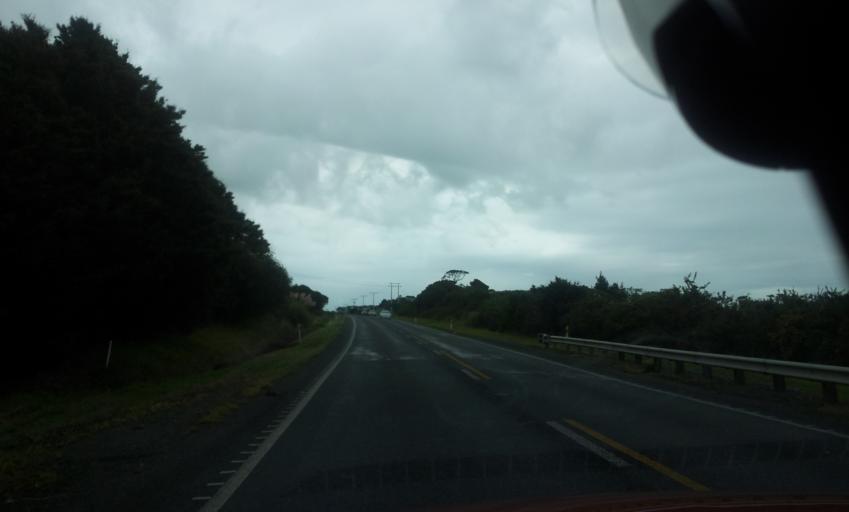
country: NZ
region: Northland
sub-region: Whangarei
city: Ruakaka
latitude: -35.9192
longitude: 174.4529
